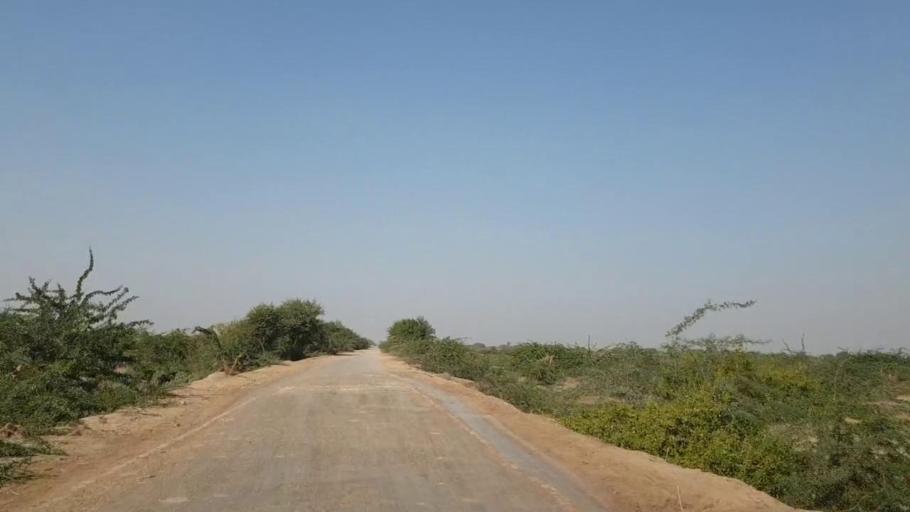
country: PK
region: Sindh
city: Digri
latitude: 24.9845
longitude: 69.1100
